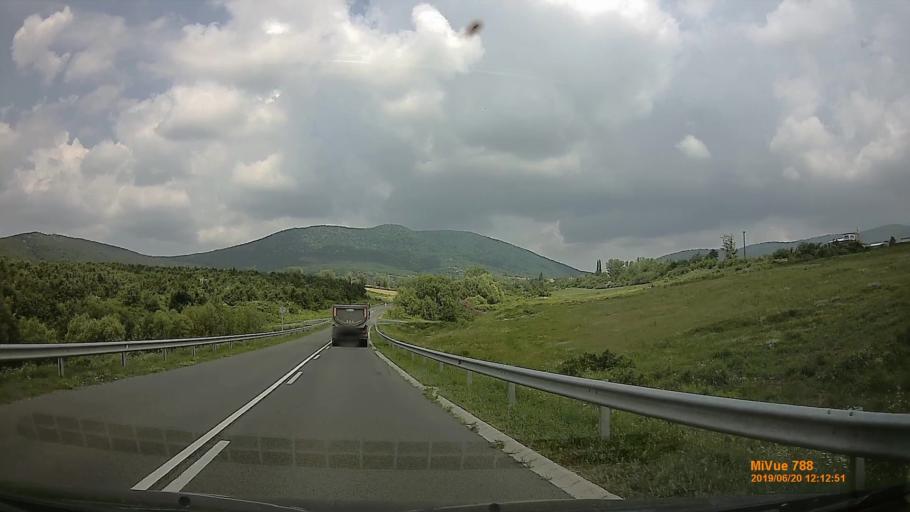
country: HU
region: Baranya
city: Hosszuheteny
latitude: 46.1515
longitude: 18.3439
